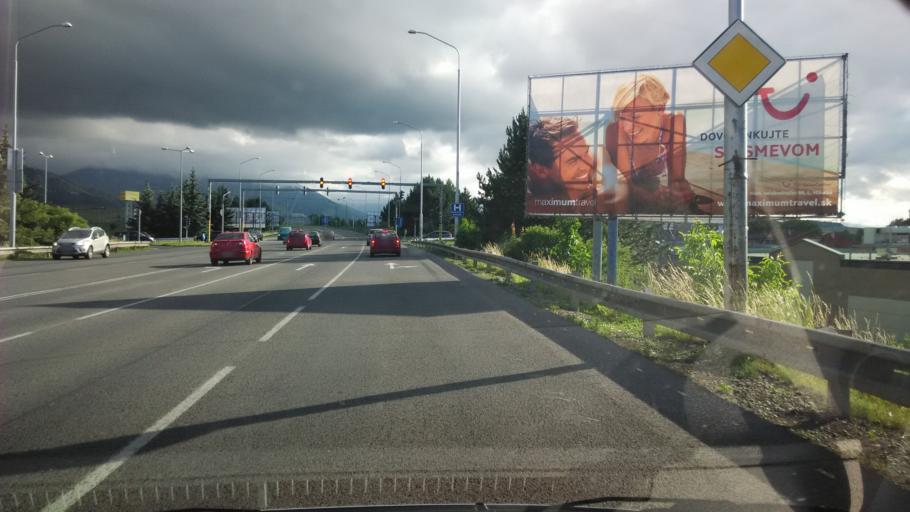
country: SK
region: Zilinsky
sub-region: Okres Liptovsky Mikulas
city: Liptovsky Mikulas
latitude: 49.0805
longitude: 19.6025
